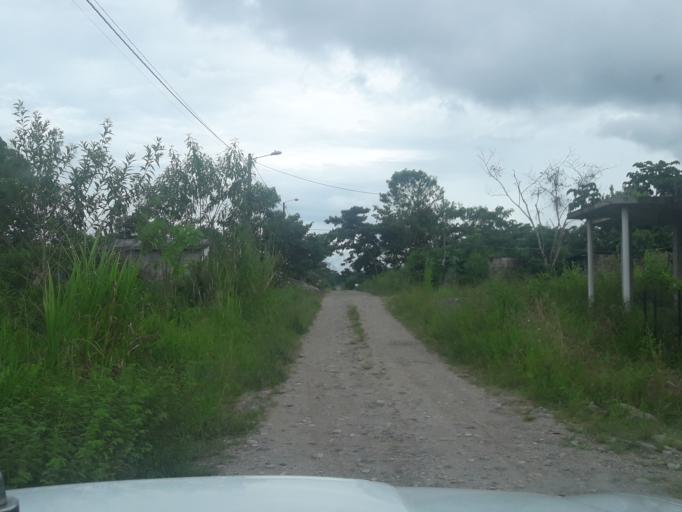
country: EC
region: Napo
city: Archidona
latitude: -0.9447
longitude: -77.8152
